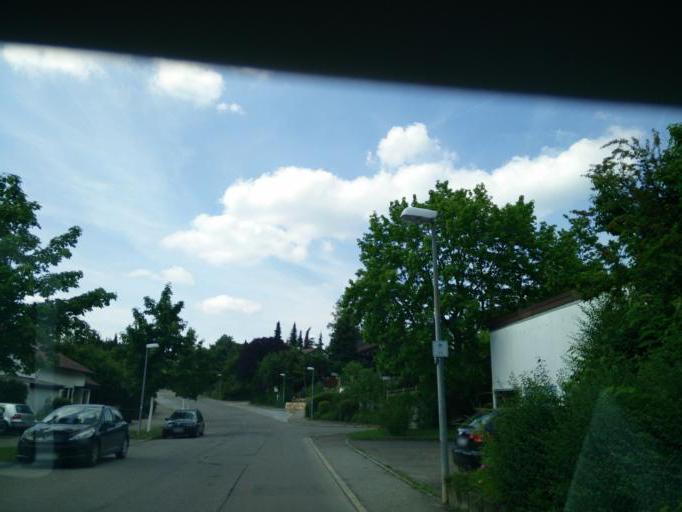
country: DE
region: Baden-Wuerttemberg
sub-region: Tuebingen Region
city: Tuebingen
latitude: 48.5386
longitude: 9.0494
